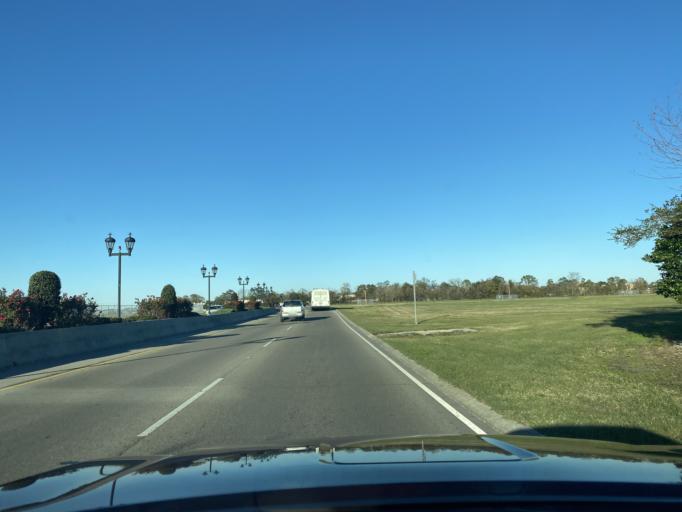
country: US
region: Louisiana
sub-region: Jefferson Parish
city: Kenner
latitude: 29.9868
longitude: -90.2489
